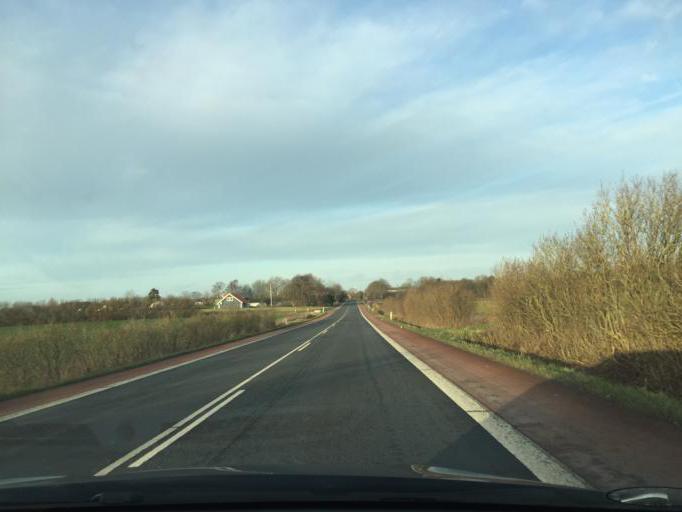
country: DK
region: South Denmark
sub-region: Faaborg-Midtfyn Kommune
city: Arslev
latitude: 55.2898
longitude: 10.4500
